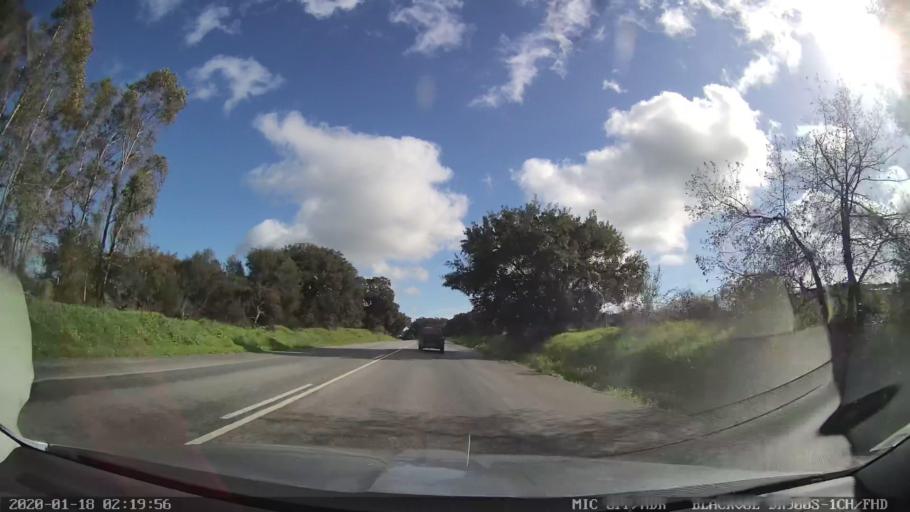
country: PT
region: Evora
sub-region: Montemor-O-Novo
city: Montemor-o-Novo
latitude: 38.6433
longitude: -8.1490
